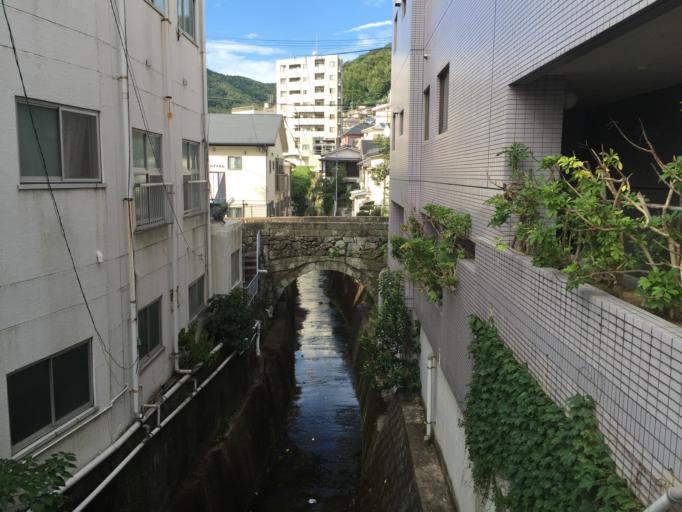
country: JP
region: Nagasaki
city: Nagasaki-shi
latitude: 32.7528
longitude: 129.8916
